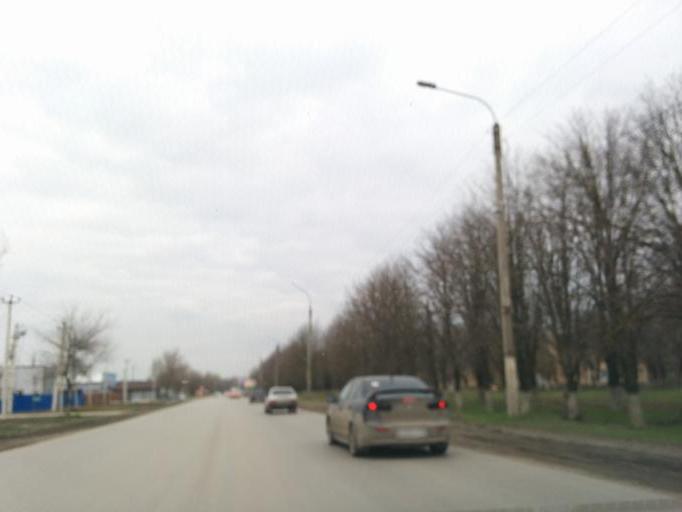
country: RU
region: Rostov
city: Novocherkassk
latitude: 47.4849
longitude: 40.1029
